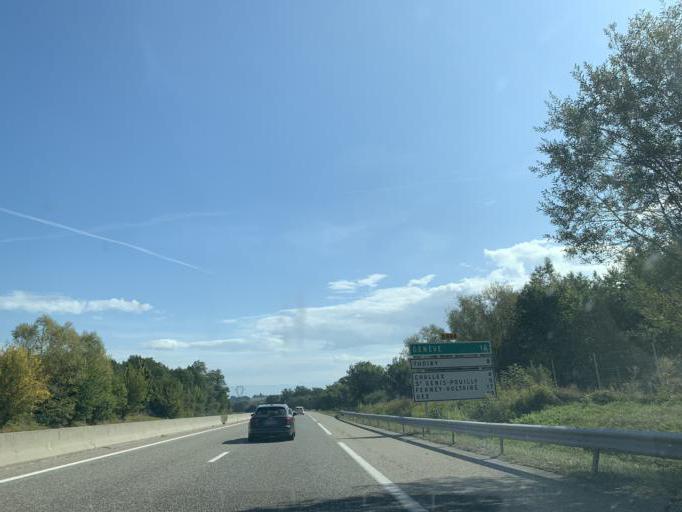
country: FR
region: Rhone-Alpes
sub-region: Departement de l'Ain
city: Peron
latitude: 46.1843
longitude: 5.9373
